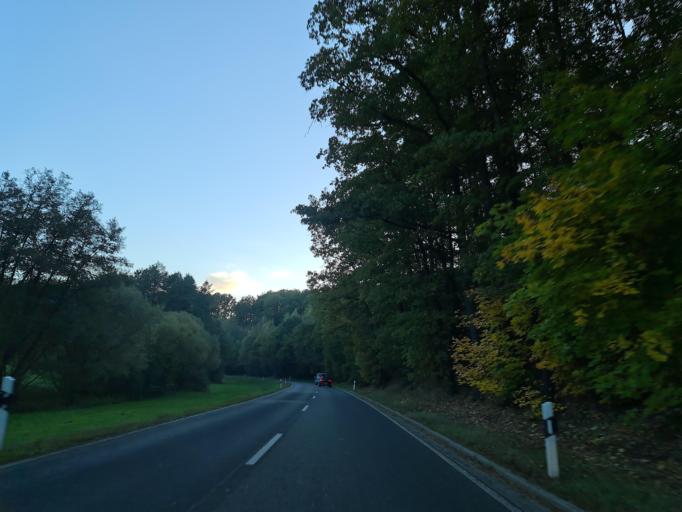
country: DE
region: Saxony
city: Elsterberg
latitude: 50.6011
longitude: 12.1409
